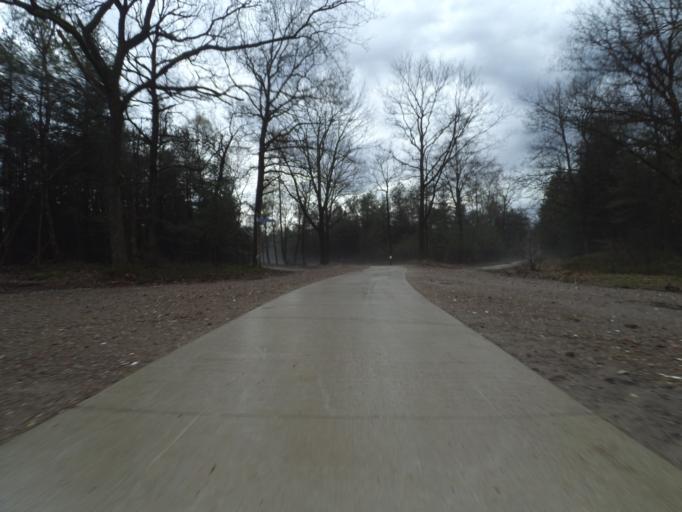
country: NL
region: Gelderland
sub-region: Gemeente Apeldoorn
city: Beekbergen
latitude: 52.1412
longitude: 5.9016
